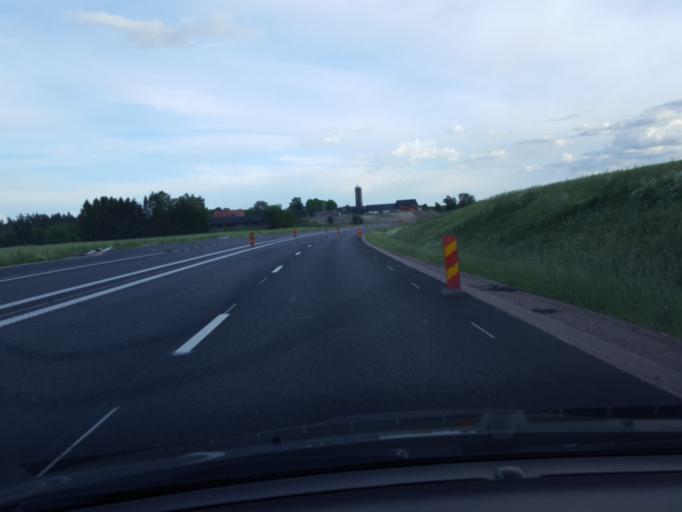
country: SE
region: Uppsala
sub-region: Osthammars Kommun
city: Gimo
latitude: 60.0877
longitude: 18.1203
